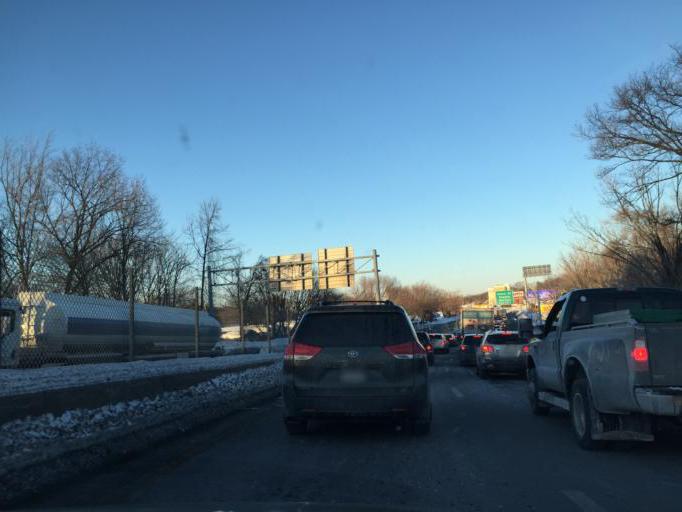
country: US
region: Massachusetts
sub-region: Essex County
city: Saugus
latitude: 42.4415
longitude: -71.0280
